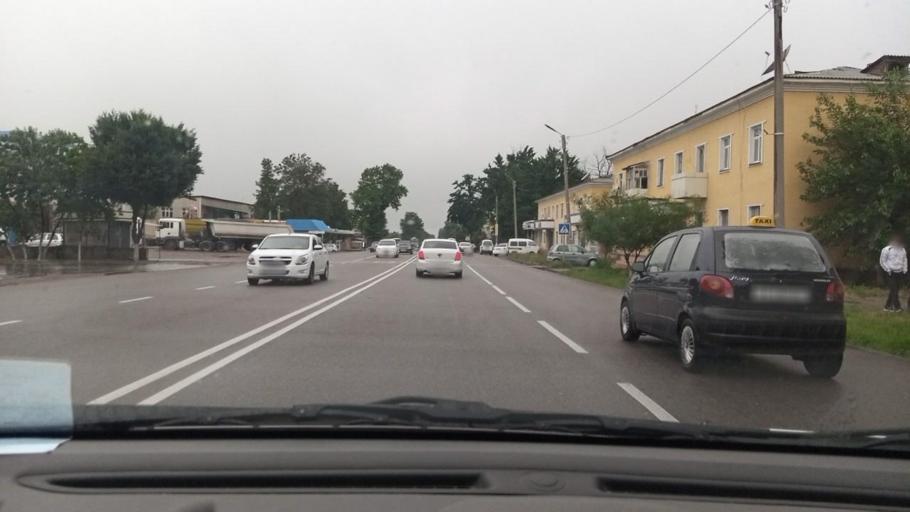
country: UZ
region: Toshkent
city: Angren
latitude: 41.0051
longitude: 70.0863
